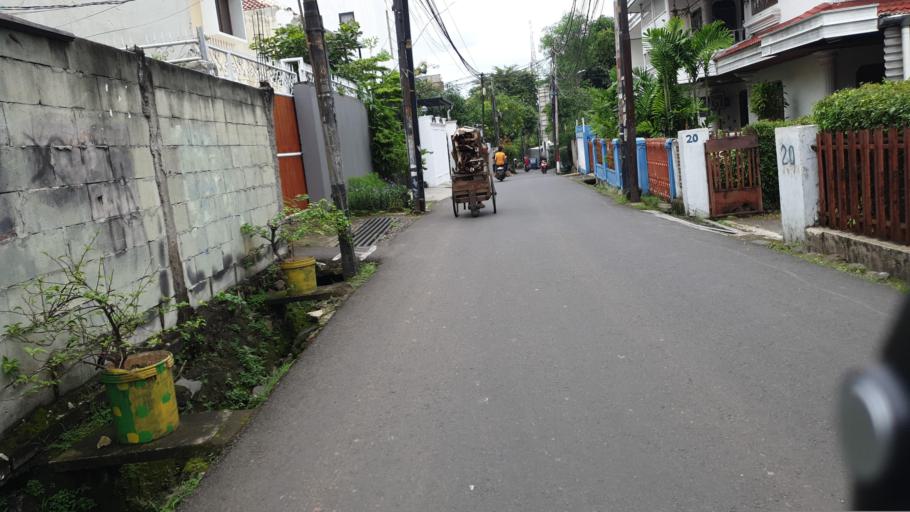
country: ID
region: Jakarta Raya
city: Jakarta
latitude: -6.2479
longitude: 106.7826
